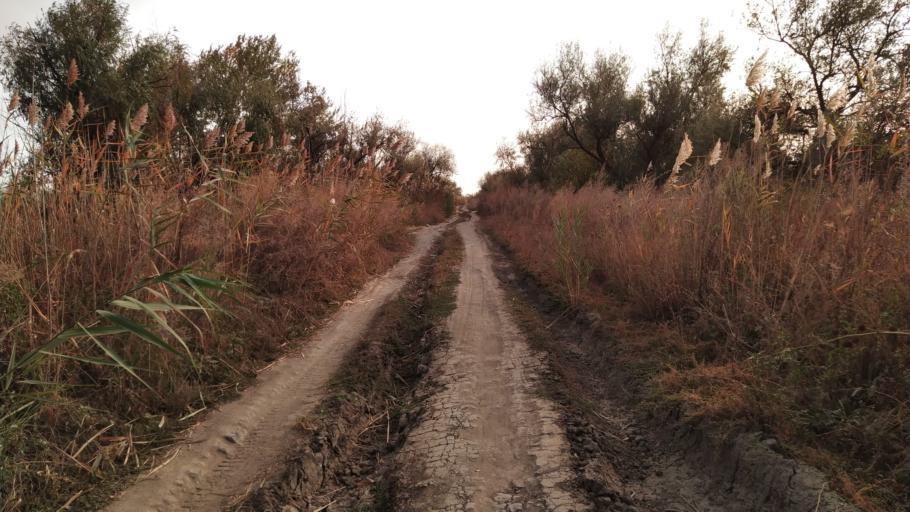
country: RU
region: Rostov
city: Kuleshovka
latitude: 47.1222
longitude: 39.6042
